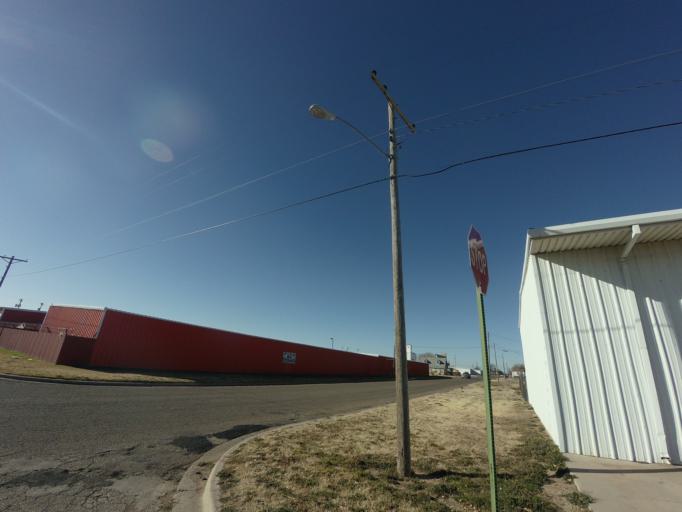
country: US
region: New Mexico
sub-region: Curry County
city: Clovis
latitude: 34.3998
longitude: -103.1902
